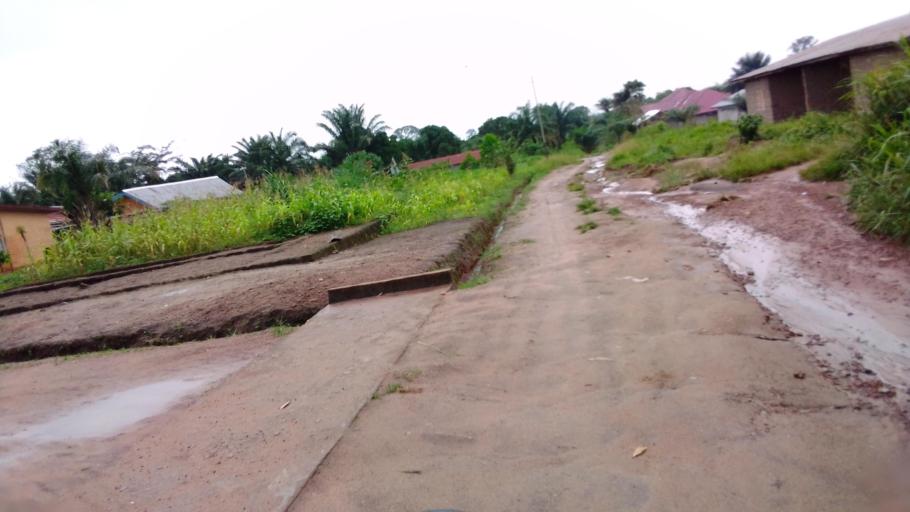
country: SL
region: Eastern Province
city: Kenema
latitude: 7.8444
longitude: -11.2045
